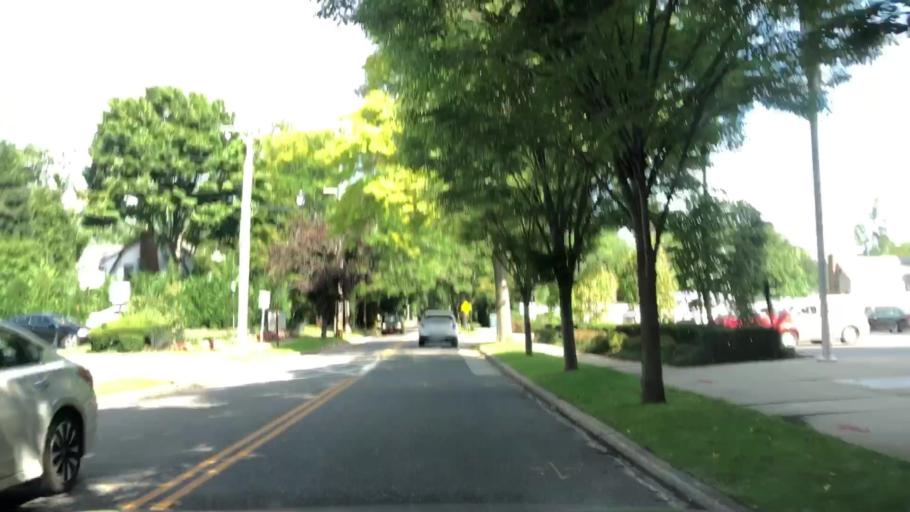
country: US
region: New York
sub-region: Nassau County
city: Manhasset
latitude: 40.7936
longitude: -73.6950
